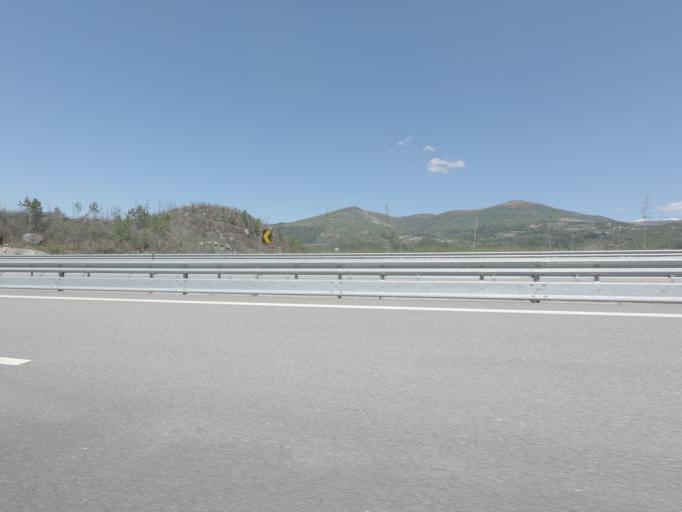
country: PT
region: Porto
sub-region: Amarante
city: Amarante
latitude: 41.2569
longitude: -7.9962
